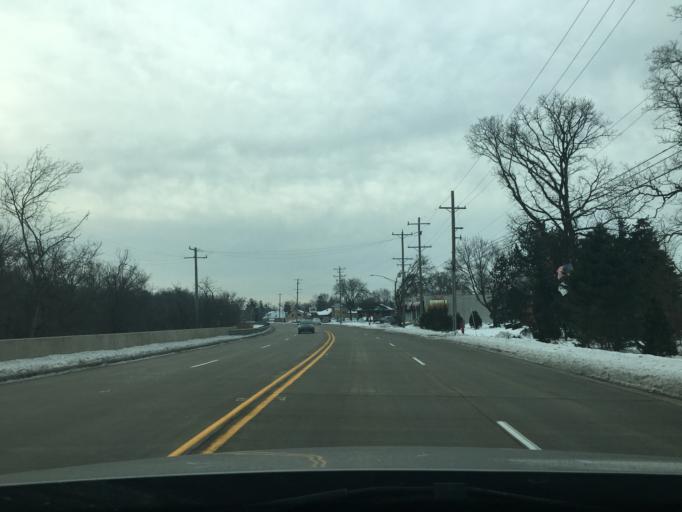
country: US
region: Illinois
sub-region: Cook County
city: Des Plaines
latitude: 42.0189
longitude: -87.8749
